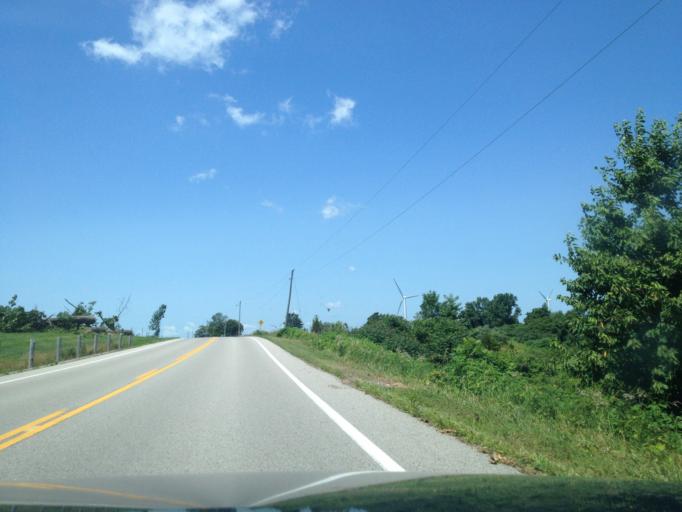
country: CA
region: Ontario
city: Norfolk County
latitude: 42.5765
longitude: -80.5471
